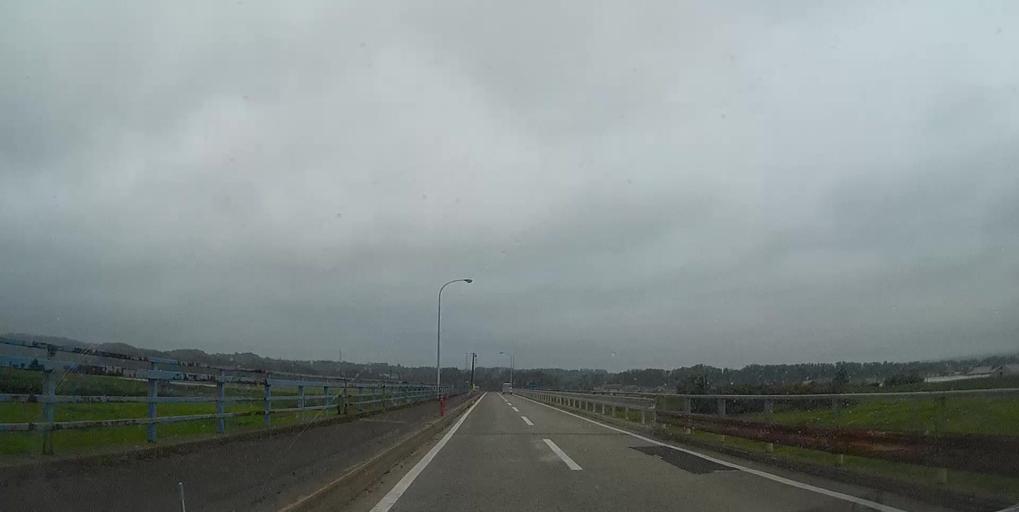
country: JP
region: Hokkaido
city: Iwanai
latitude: 42.4206
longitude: 140.0206
